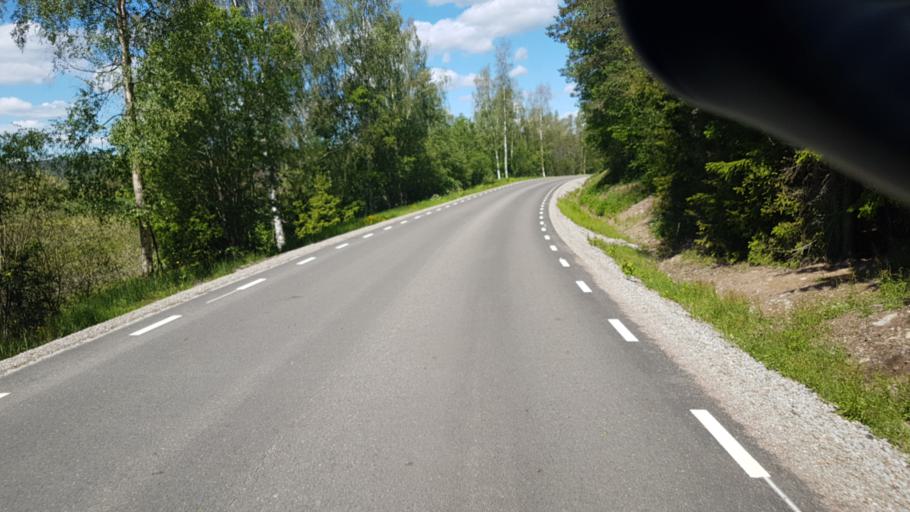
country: SE
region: Vaermland
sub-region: Arvika Kommun
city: Arvika
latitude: 59.6580
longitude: 12.8006
